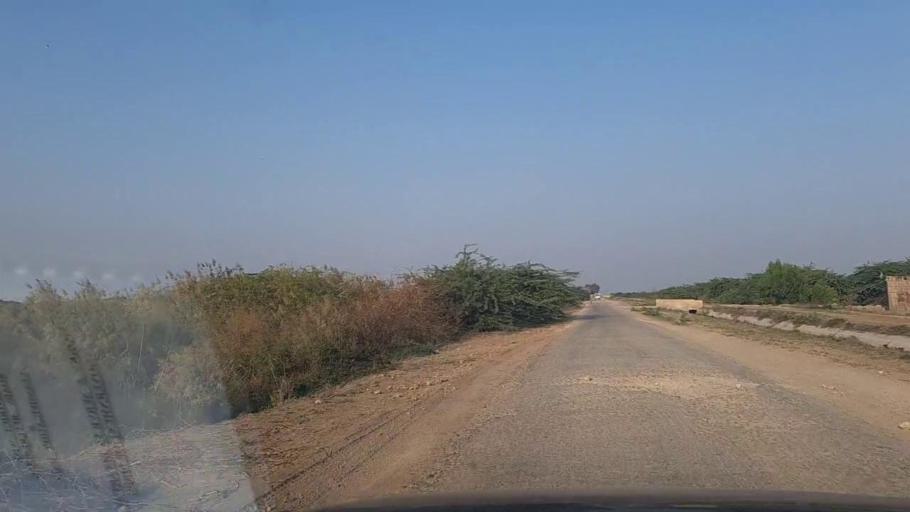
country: PK
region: Sindh
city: Keti Bandar
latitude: 24.2591
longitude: 67.5413
